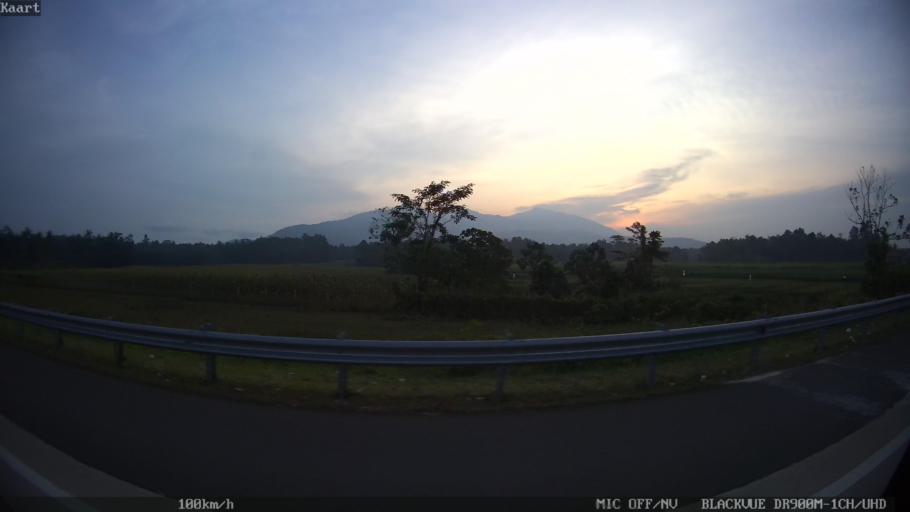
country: ID
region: Lampung
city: Penengahan
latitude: -5.7640
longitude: 105.7135
